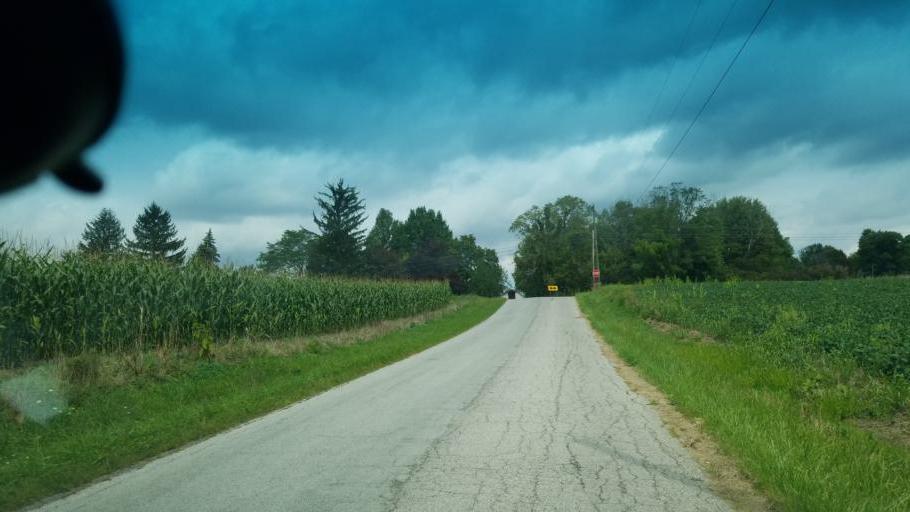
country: US
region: Ohio
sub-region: Richland County
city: Ontario
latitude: 40.8131
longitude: -82.5710
